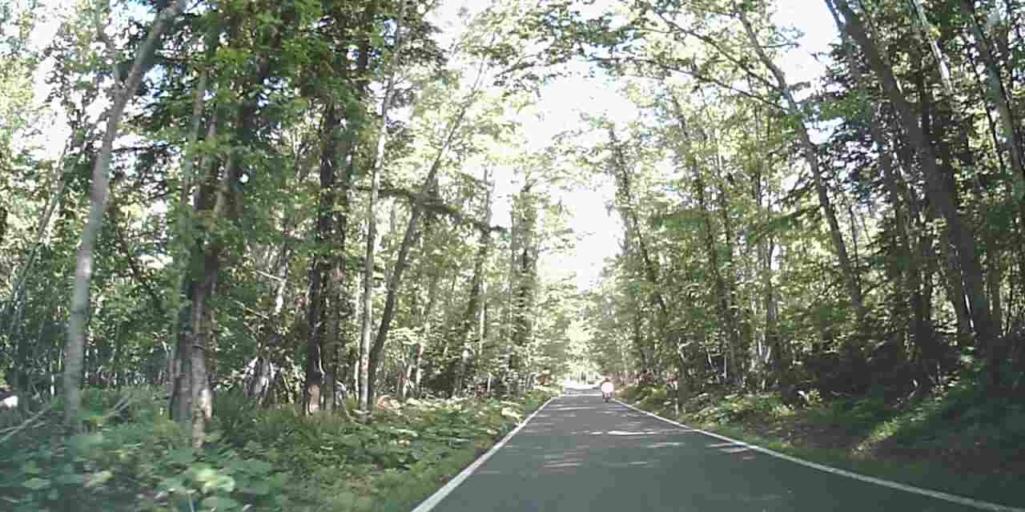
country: JP
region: Hokkaido
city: Shiraoi
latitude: 42.7311
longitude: 141.4130
